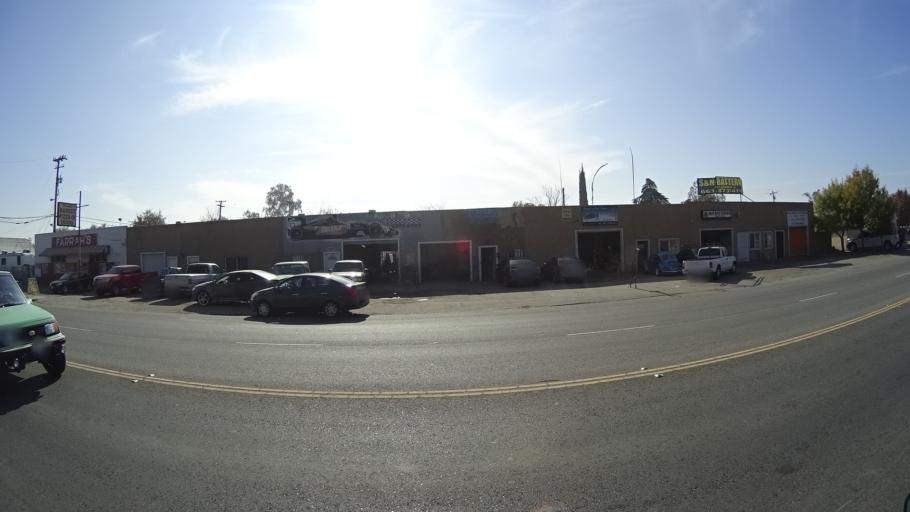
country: US
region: California
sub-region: Kern County
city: Bakersfield
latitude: 35.3539
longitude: -118.9985
